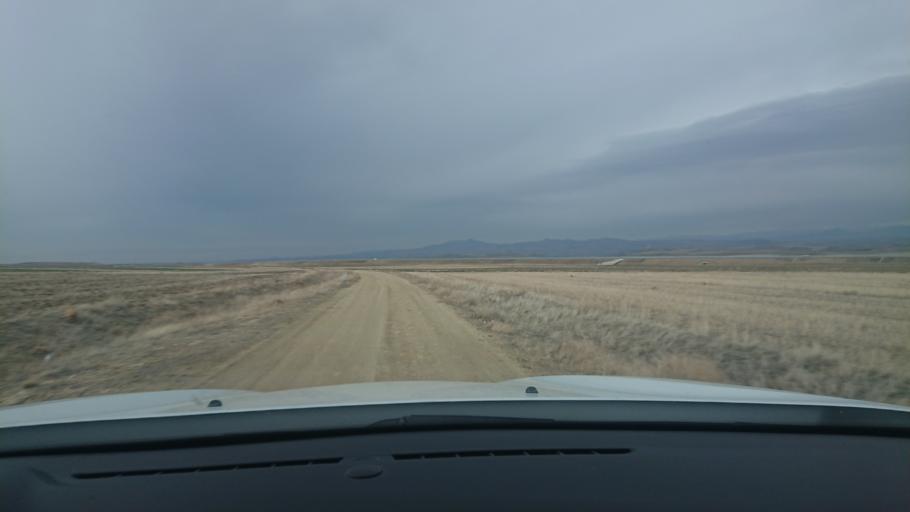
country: TR
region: Aksaray
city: Sariyahsi
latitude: 38.9827
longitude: 33.8771
